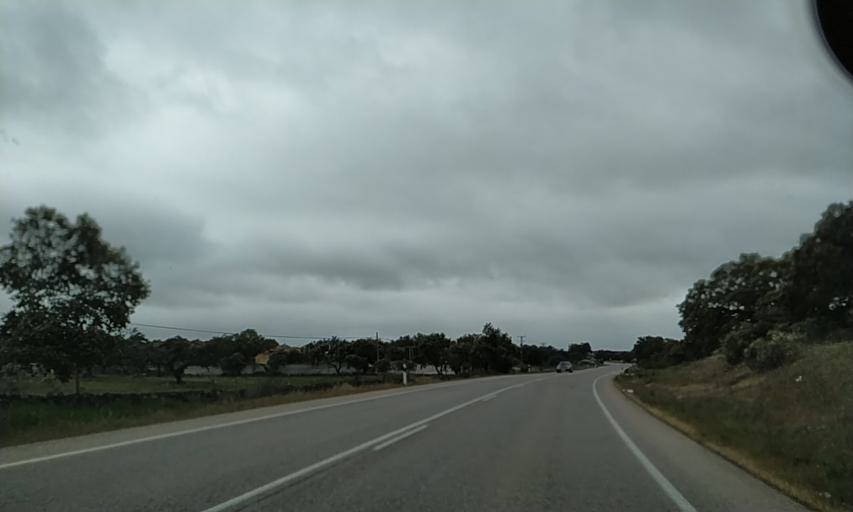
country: ES
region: Extremadura
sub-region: Provincia de Caceres
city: Caceres
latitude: 39.3984
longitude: -6.4225
